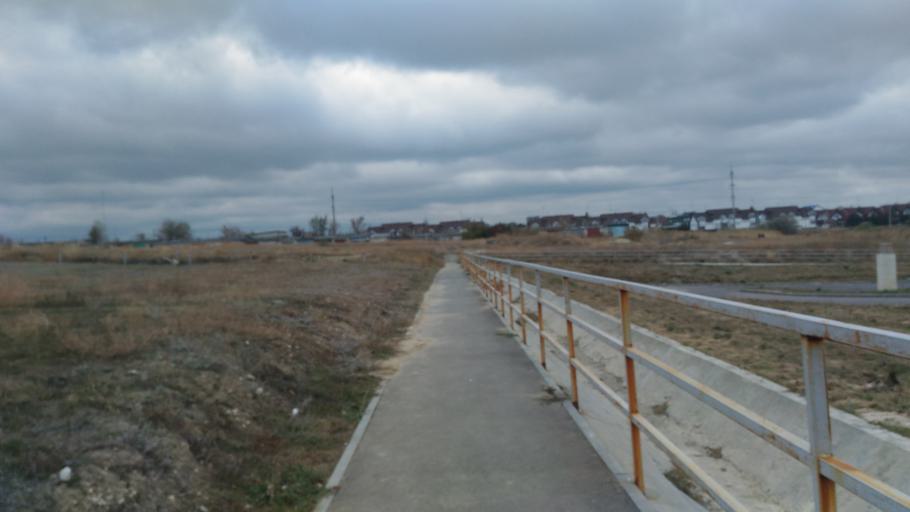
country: RU
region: Volgograd
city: Volgograd
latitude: 48.6425
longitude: 44.4233
